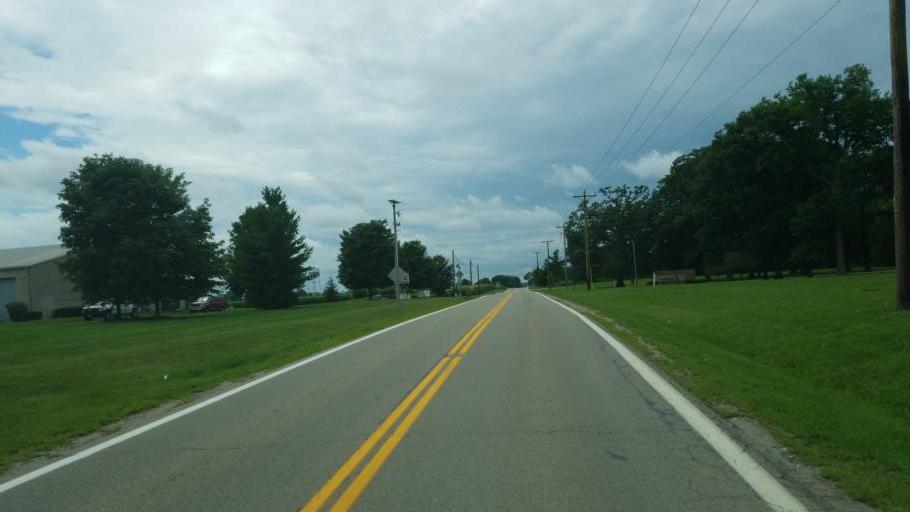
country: US
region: Ohio
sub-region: Pickaway County
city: Ashville
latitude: 39.7238
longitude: -82.9623
